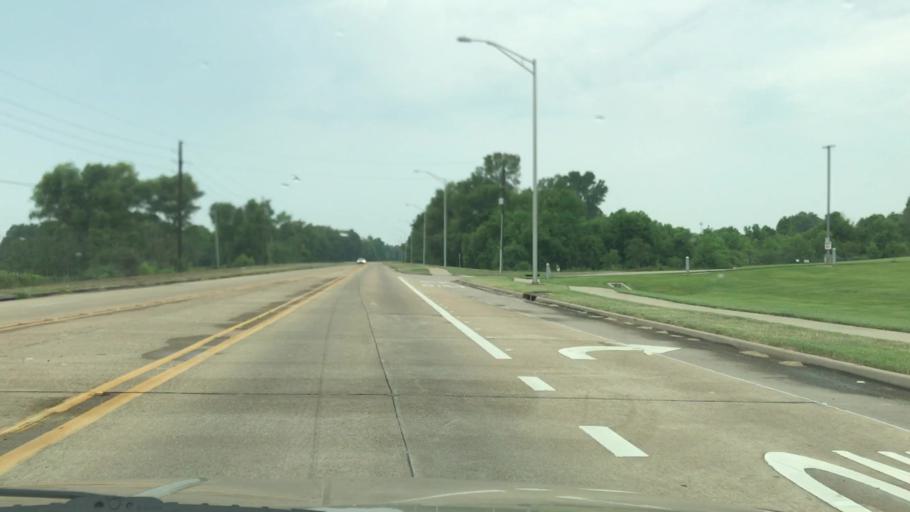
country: US
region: Louisiana
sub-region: Bossier Parish
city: Bossier City
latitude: 32.4754
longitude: -93.6947
